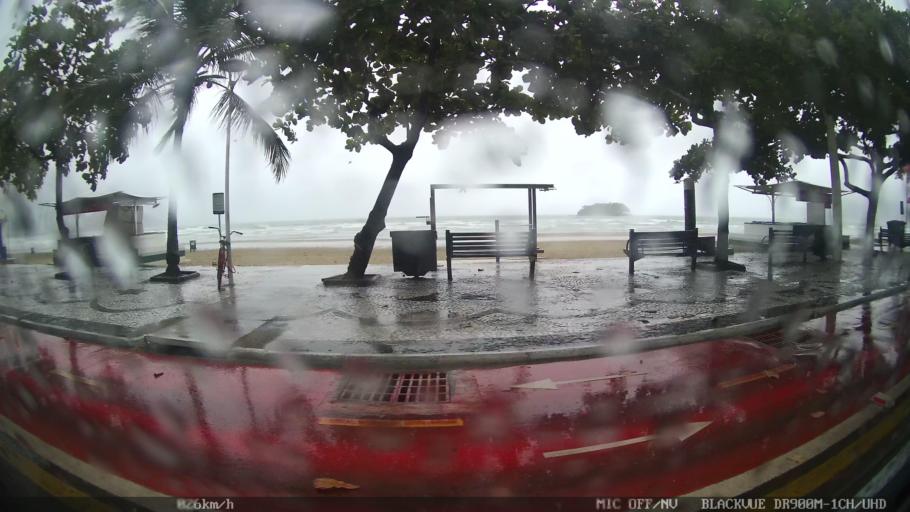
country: BR
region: Santa Catarina
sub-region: Balneario Camboriu
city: Balneario Camboriu
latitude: -26.9883
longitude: -48.6307
